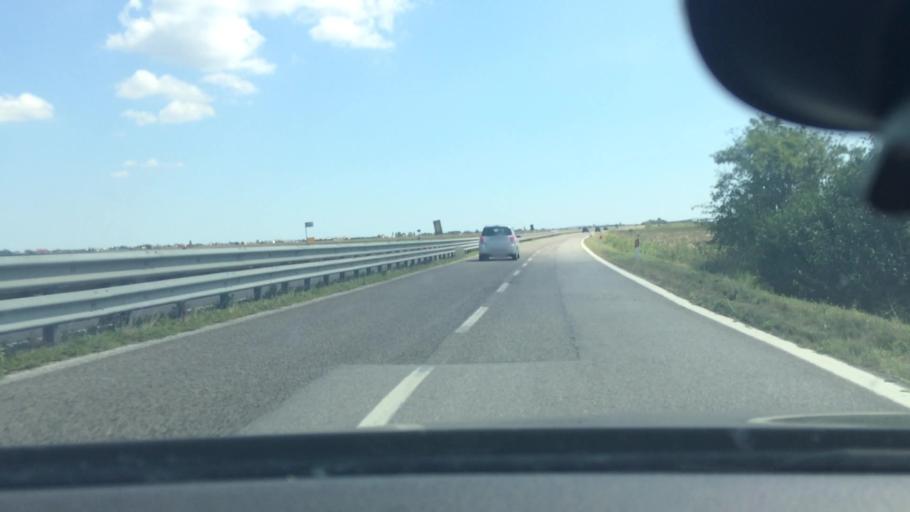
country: IT
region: Emilia-Romagna
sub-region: Provincia di Ferrara
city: Ostellato
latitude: 44.7562
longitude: 11.9681
